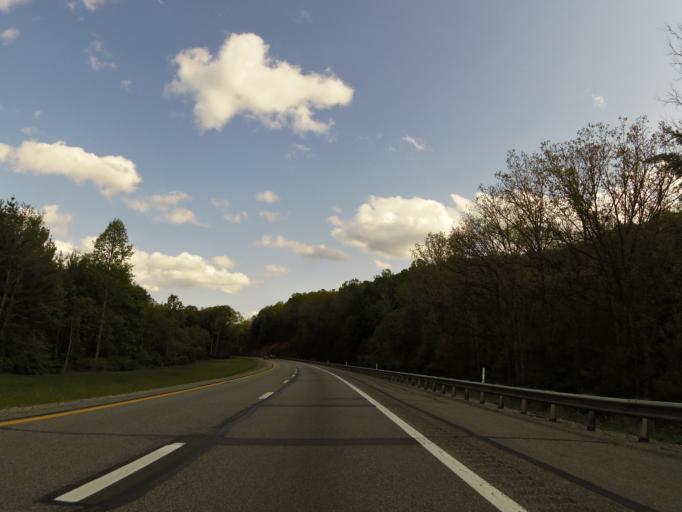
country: US
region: West Virginia
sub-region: Raleigh County
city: Beaver
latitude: 37.7064
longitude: -81.1517
